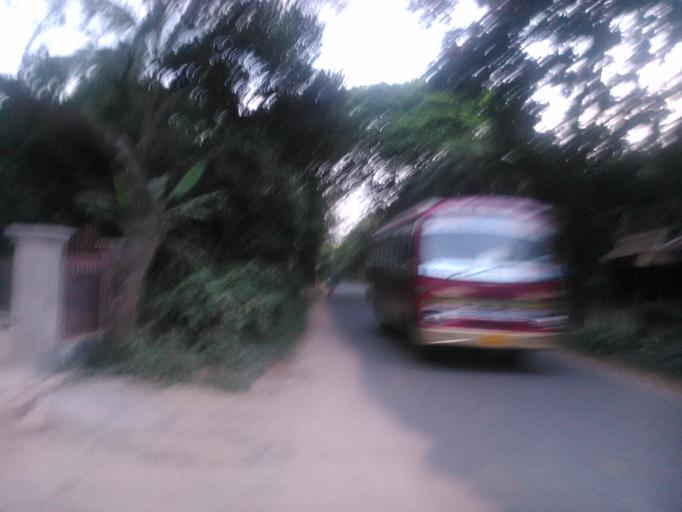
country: IN
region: West Bengal
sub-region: Nadia
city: Navadwip
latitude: 23.4332
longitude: 88.3894
